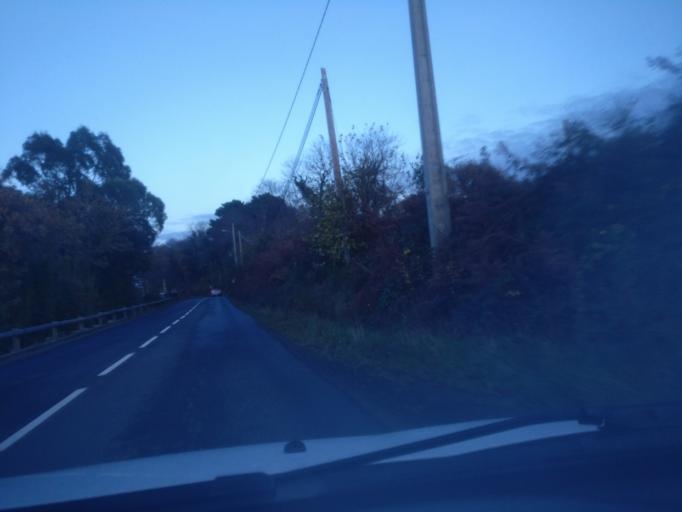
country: FR
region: Brittany
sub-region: Departement des Cotes-d'Armor
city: Saint-Quay-Perros
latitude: 48.7981
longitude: -3.4562
